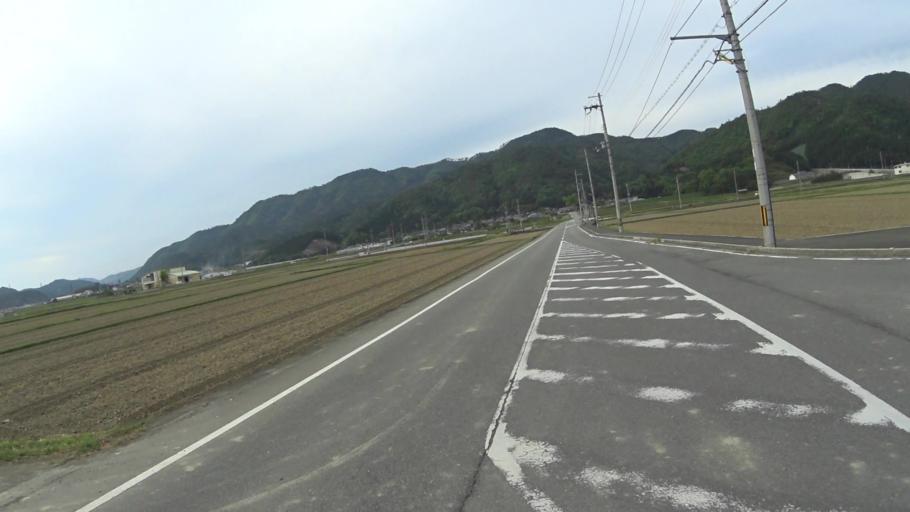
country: JP
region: Kyoto
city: Kameoka
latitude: 35.0895
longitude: 135.5475
